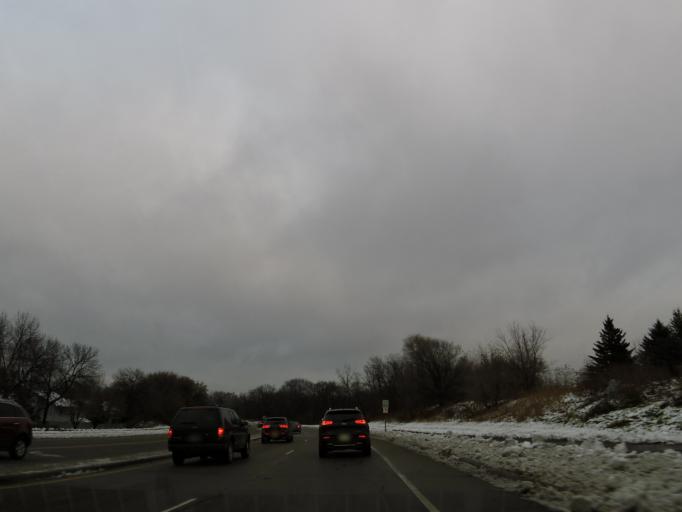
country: US
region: Minnesota
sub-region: Dakota County
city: Apple Valley
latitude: 44.7138
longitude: -93.2597
